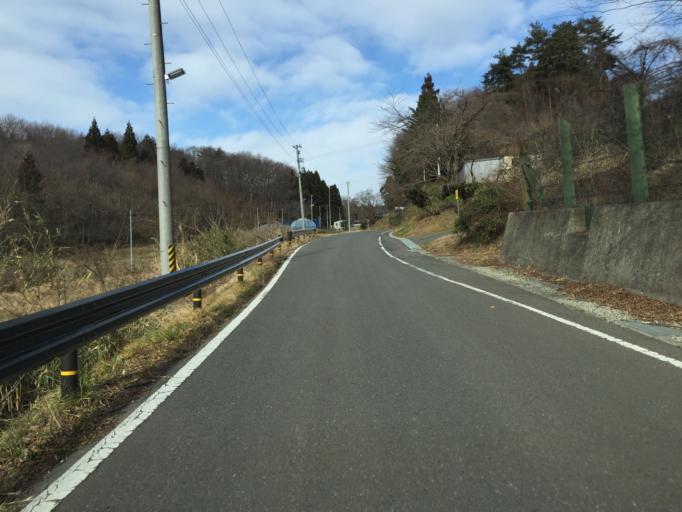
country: JP
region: Fukushima
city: Fukushima-shi
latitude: 37.7108
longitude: 140.5527
